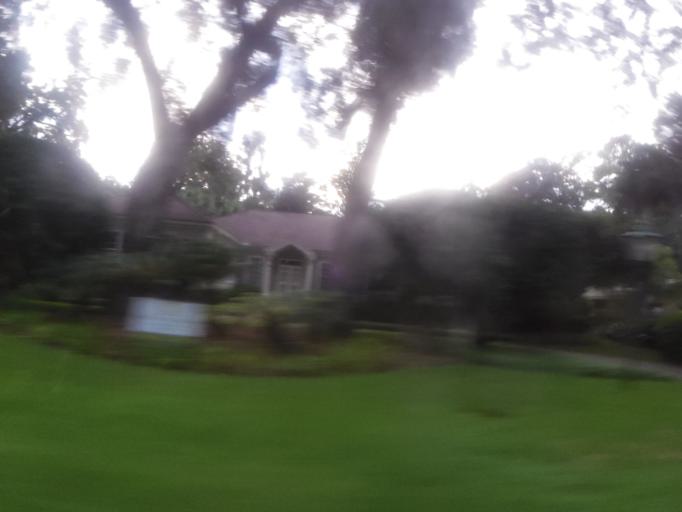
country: US
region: Florida
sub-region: Duval County
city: Jacksonville
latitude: 30.2658
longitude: -81.6998
